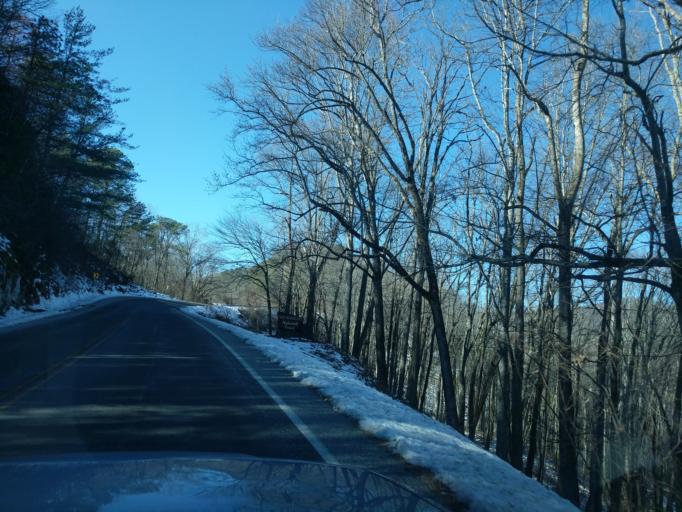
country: US
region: Georgia
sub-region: Towns County
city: Hiawassee
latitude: 34.8915
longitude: -83.5851
